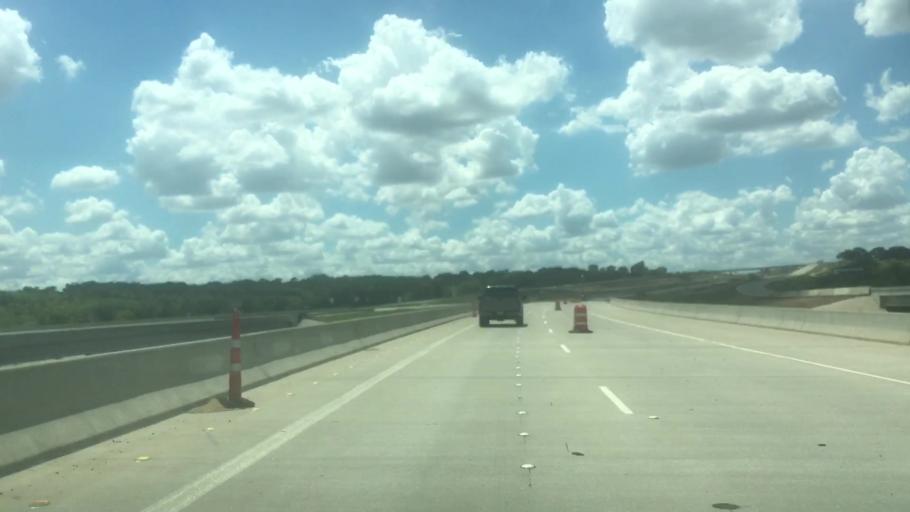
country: US
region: Texas
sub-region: Caldwell County
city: Lockhart
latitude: 29.8597
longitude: -97.7103
